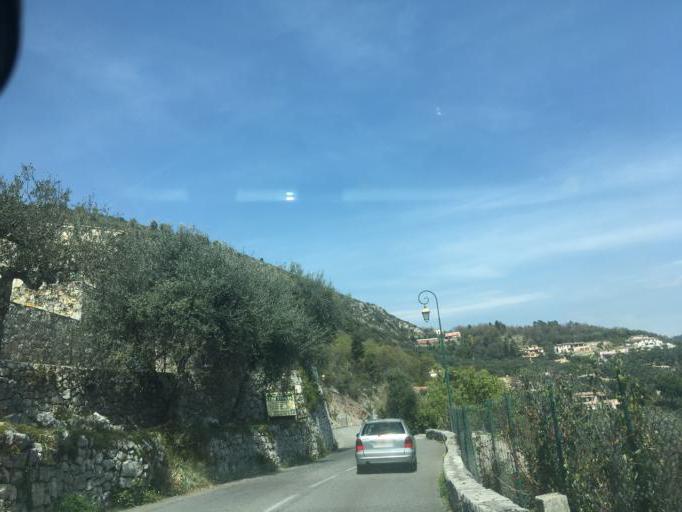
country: FR
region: Provence-Alpes-Cote d'Azur
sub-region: Departement des Alpes-Maritimes
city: Levens
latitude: 43.8425
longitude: 7.2148
